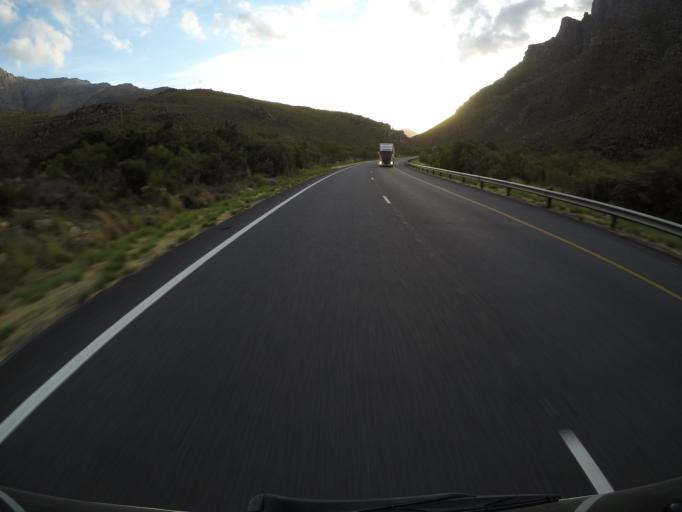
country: ZA
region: Western Cape
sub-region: Cape Winelands District Municipality
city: Paarl
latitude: -33.7203
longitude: 19.1895
